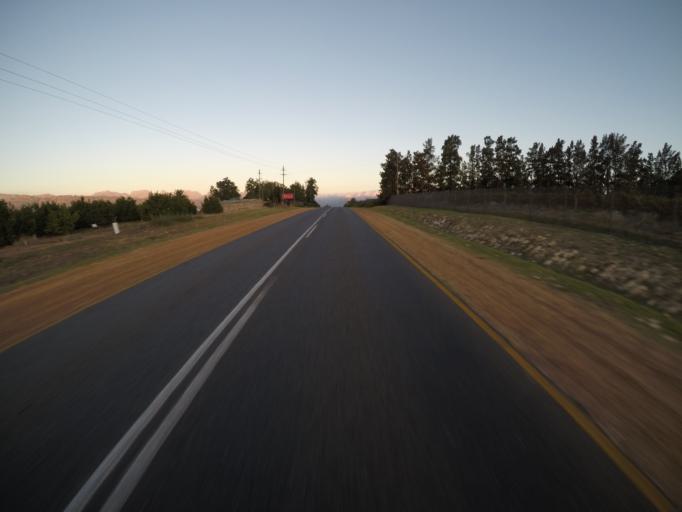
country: ZA
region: Western Cape
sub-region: Cape Winelands District Municipality
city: Paarl
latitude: -33.8280
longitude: 18.9401
